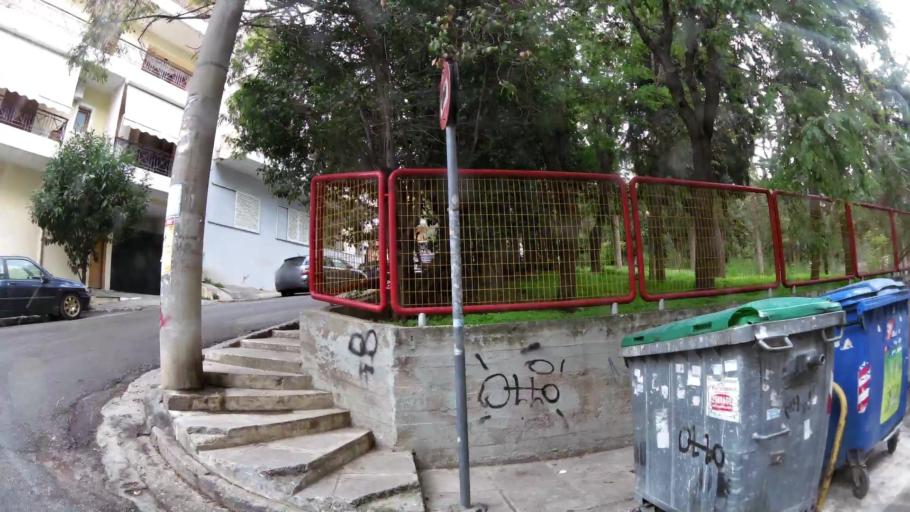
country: GR
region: Attica
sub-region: Nomarchia Athinas
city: Kaisariani
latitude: 37.9654
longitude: 23.7694
